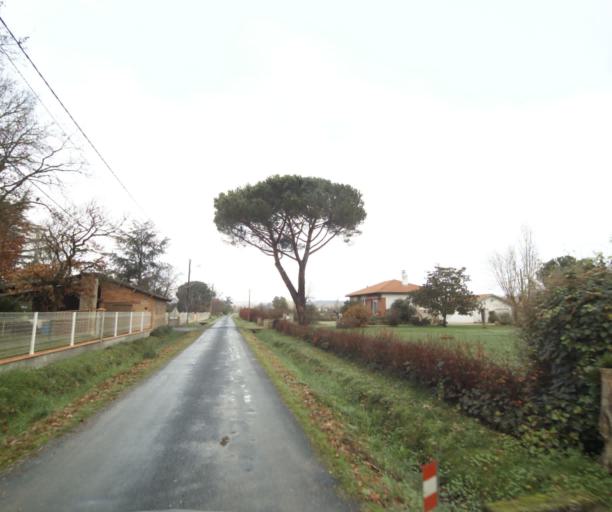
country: FR
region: Midi-Pyrenees
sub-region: Departement de la Haute-Garonne
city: Villemur-sur-Tarn
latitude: 43.8686
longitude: 1.4814
